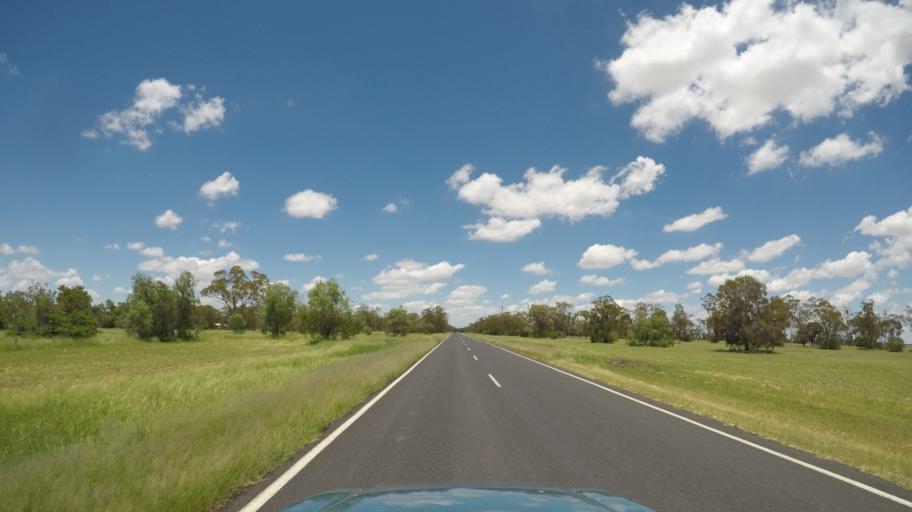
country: AU
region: Queensland
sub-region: Goondiwindi
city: Goondiwindi
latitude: -28.1754
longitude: 150.2846
